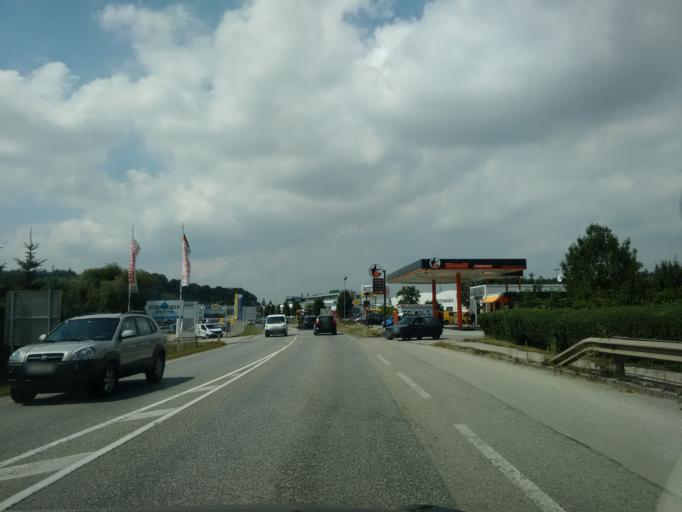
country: AT
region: Upper Austria
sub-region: Politischer Bezirk Grieskirchen
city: Grieskirchen
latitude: 48.2262
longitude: 13.8473
